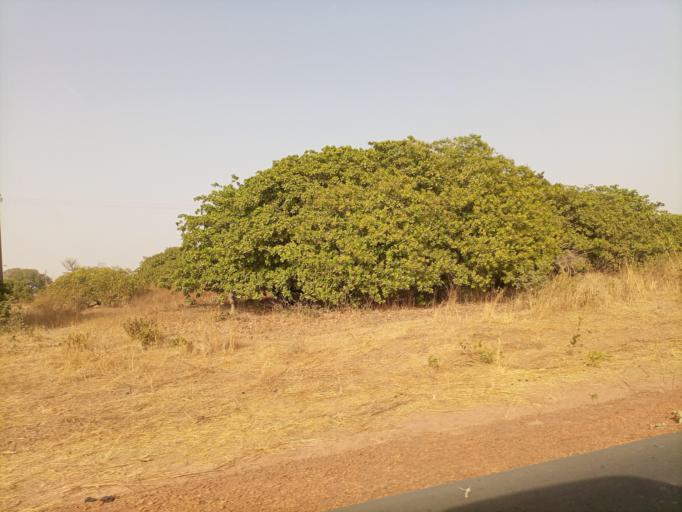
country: SN
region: Fatick
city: Passi
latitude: 14.0432
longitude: -16.3236
